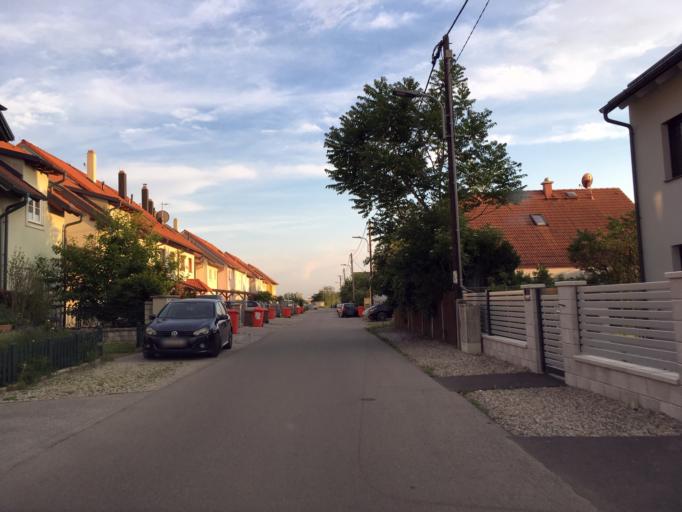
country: AT
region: Lower Austria
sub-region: Politischer Bezirk Wien-Umgebung
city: Gerasdorf bei Wien
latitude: 48.3115
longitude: 16.5009
